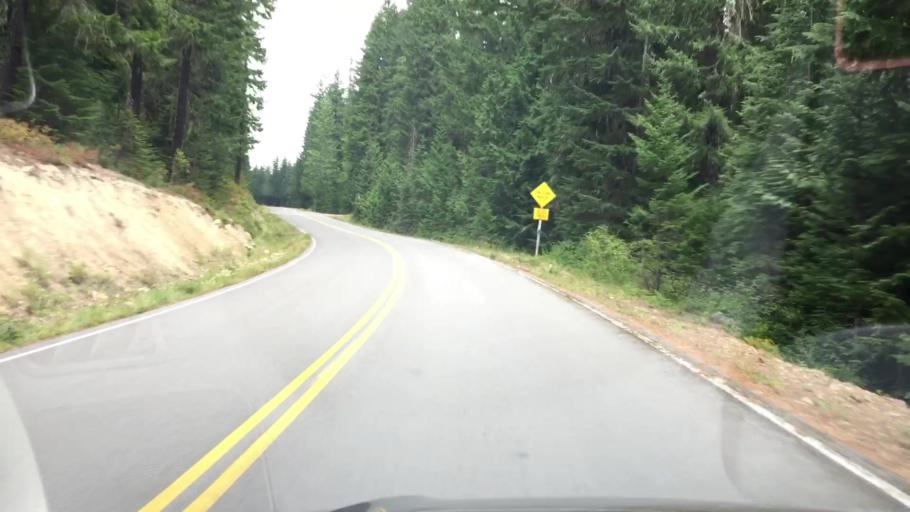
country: US
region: Washington
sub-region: Klickitat County
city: White Salmon
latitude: 46.1447
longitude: -121.6270
